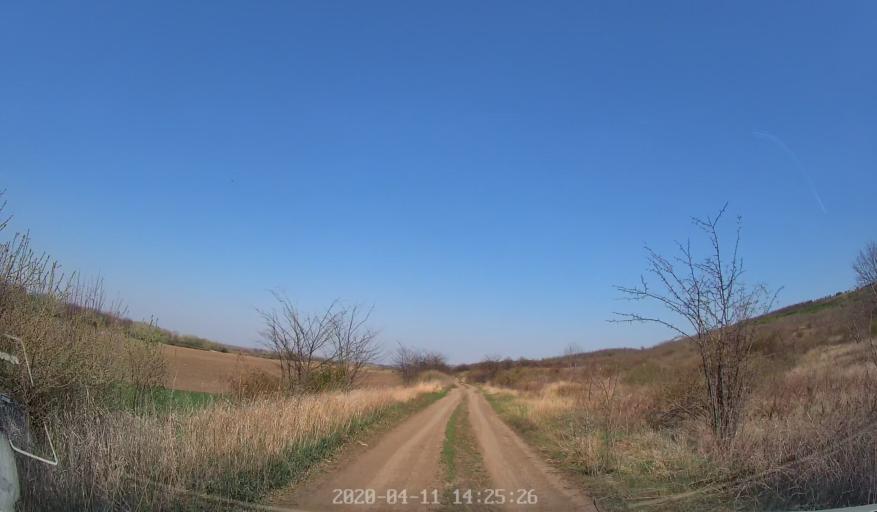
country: MD
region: Chisinau
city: Vadul lui Voda
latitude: 47.0933
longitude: 29.1457
